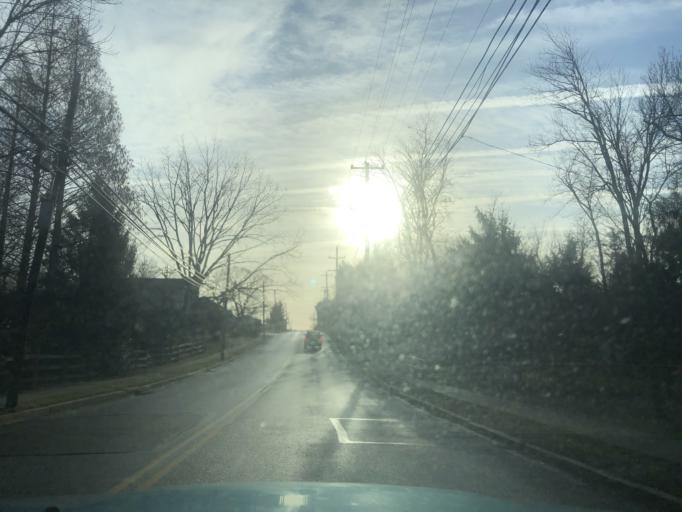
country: US
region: Pennsylvania
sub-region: Montgomery County
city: Fort Washington
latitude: 40.1452
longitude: -75.1990
